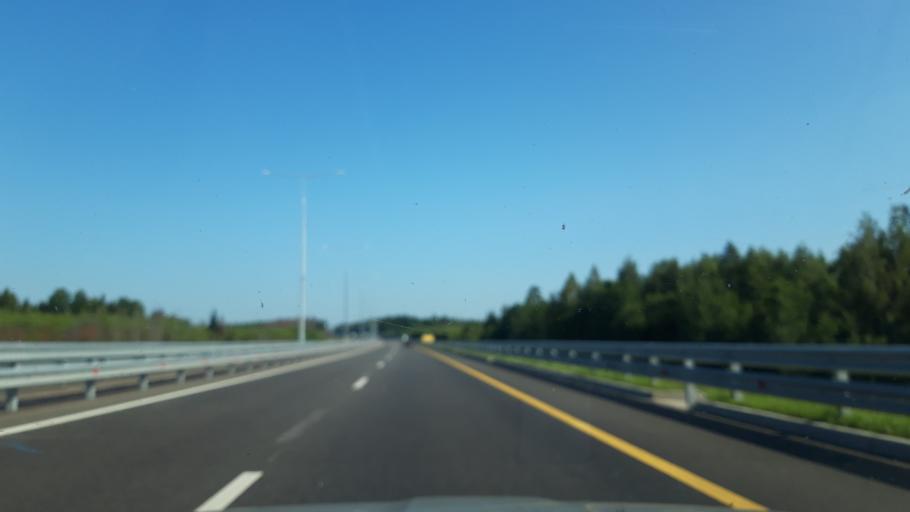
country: RU
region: Moskovskaya
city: Spas-Zaulok
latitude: 56.4758
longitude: 36.5398
